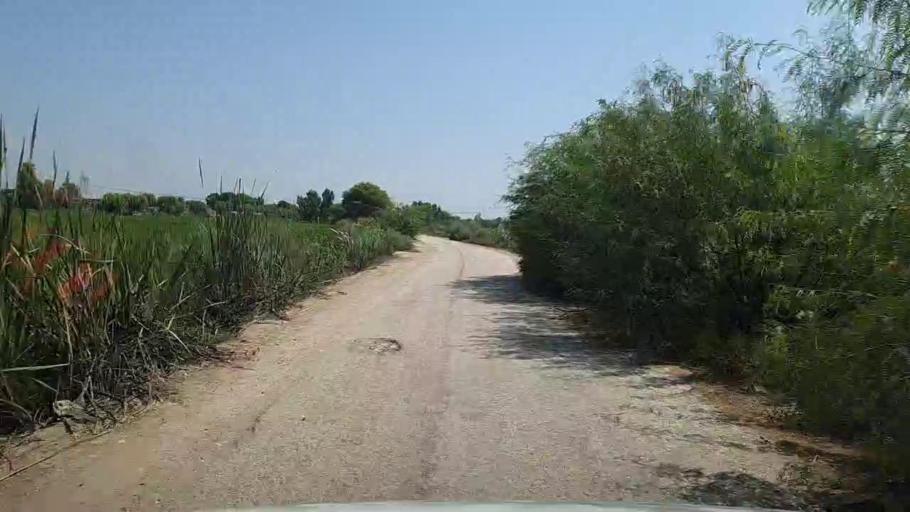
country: PK
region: Sindh
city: Kandhkot
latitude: 28.2912
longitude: 69.3517
